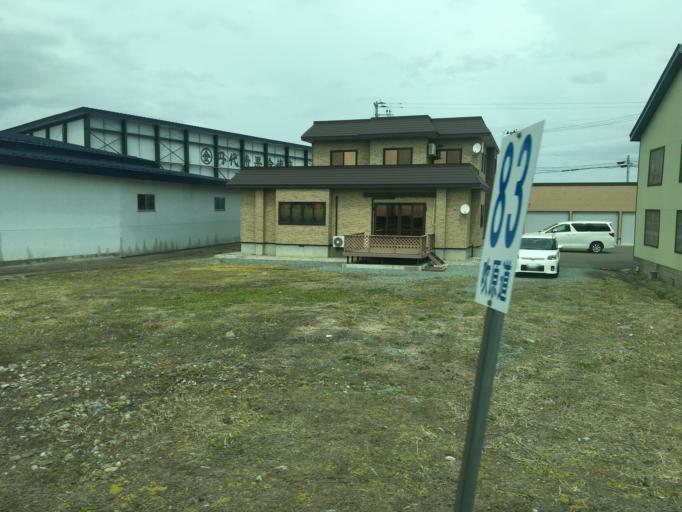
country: JP
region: Aomori
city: Shimokizukuri
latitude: 40.7821
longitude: 140.3355
